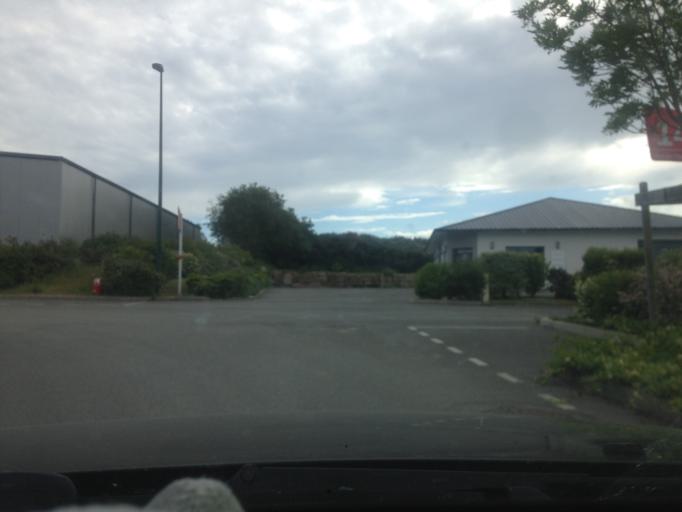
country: FR
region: Brittany
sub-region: Departement du Morbihan
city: Carnac
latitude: 47.5888
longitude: -3.0614
